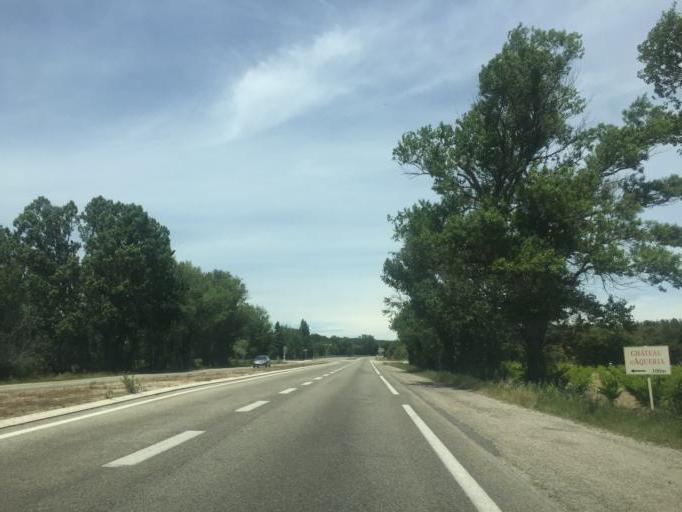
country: FR
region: Languedoc-Roussillon
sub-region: Departement du Gard
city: Tavel
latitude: 44.0063
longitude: 4.7357
